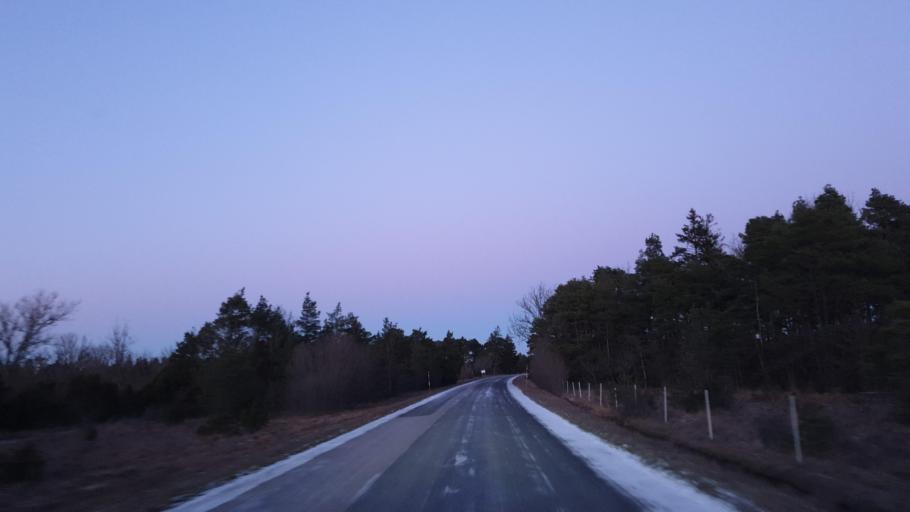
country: SE
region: Gotland
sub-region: Gotland
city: Slite
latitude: 57.4093
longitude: 18.8071
